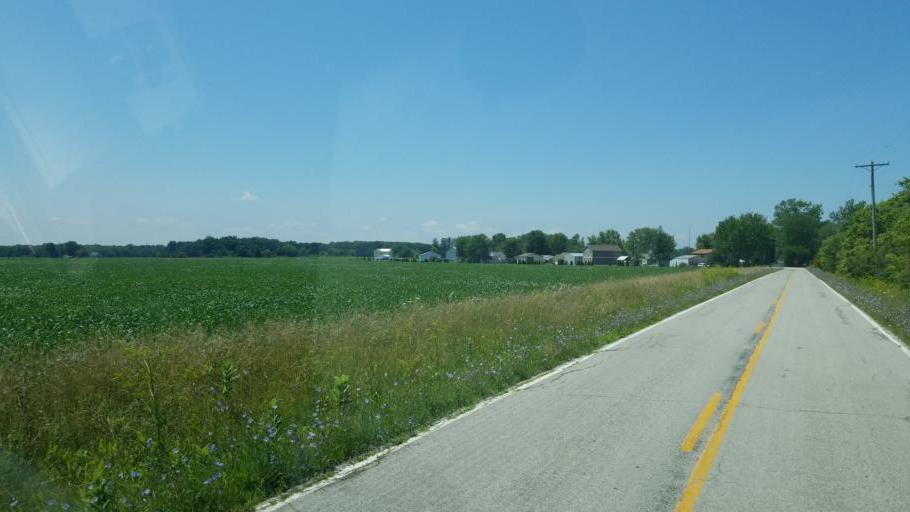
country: US
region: Ohio
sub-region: Sandusky County
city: Fremont
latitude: 41.4217
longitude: -83.0577
